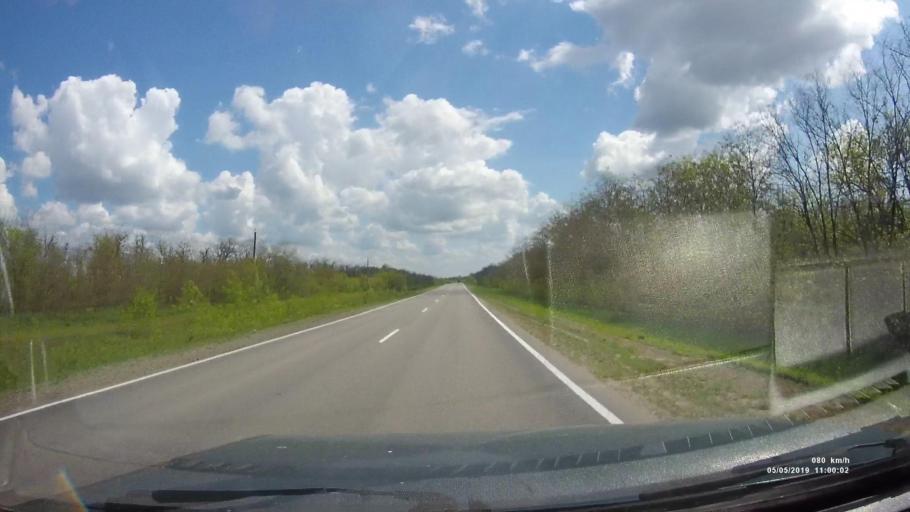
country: RU
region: Rostov
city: Ust'-Donetskiy
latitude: 47.6725
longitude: 40.8781
